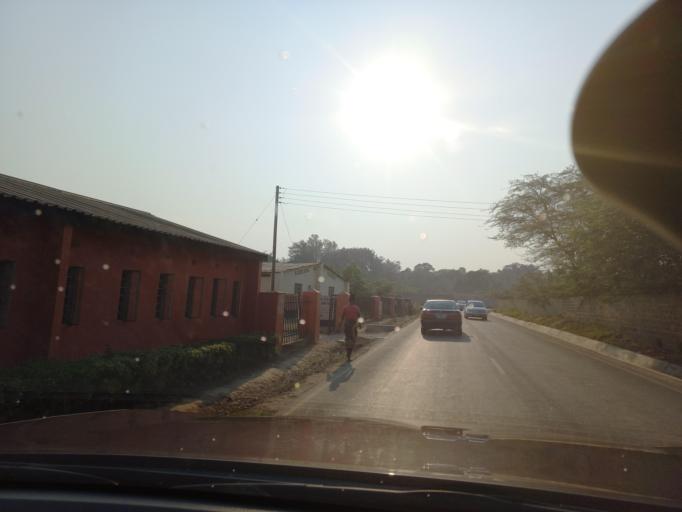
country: ZM
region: Lusaka
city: Lusaka
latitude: -15.4160
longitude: 28.3583
